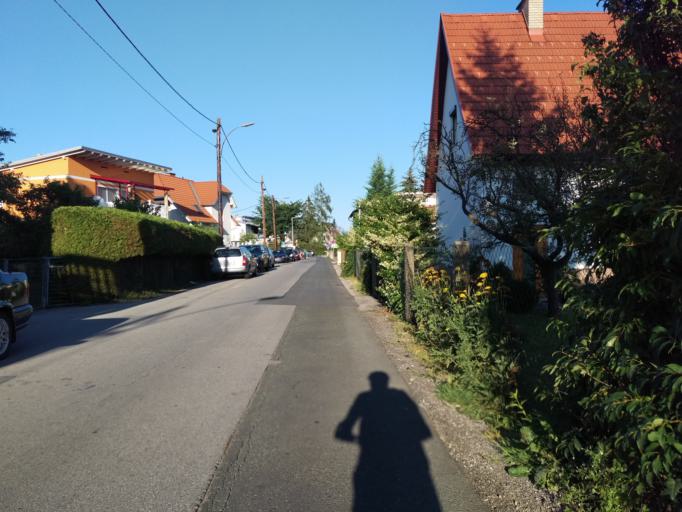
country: AT
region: Styria
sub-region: Graz Stadt
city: Wetzelsdorf
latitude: 47.0466
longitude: 15.4130
